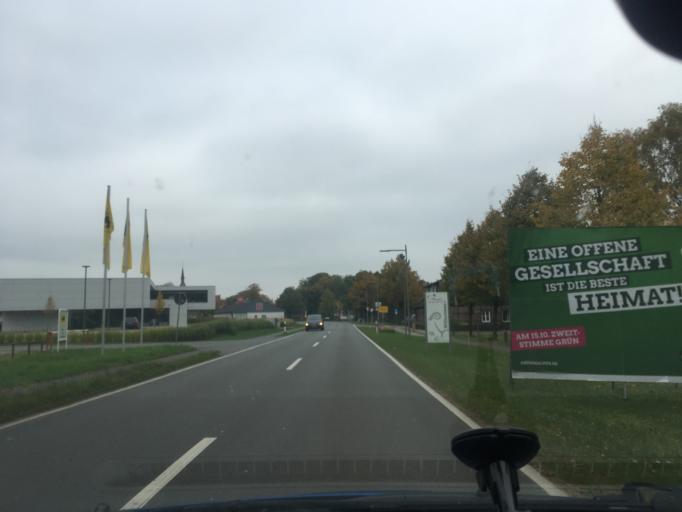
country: DE
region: Lower Saxony
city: Bispingen
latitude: 53.0782
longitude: 9.9957
